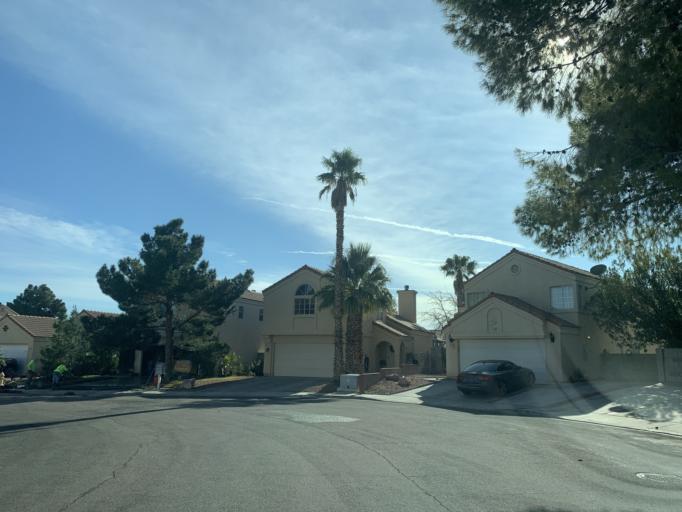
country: US
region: Nevada
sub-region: Clark County
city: Summerlin South
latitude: 36.1315
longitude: -115.2928
